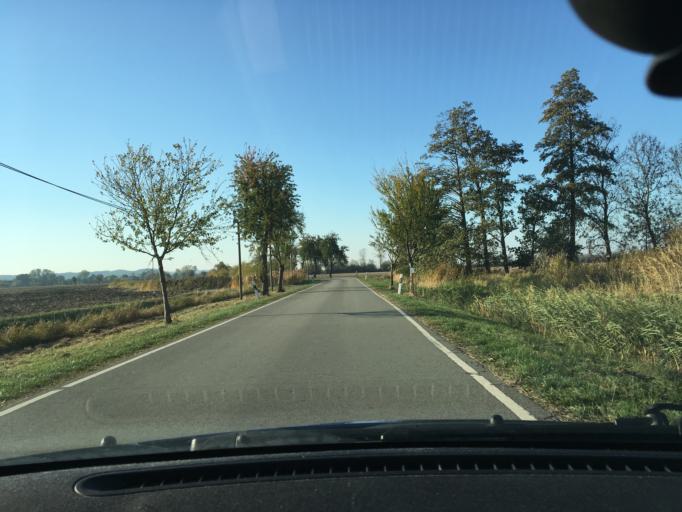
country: DE
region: Lower Saxony
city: Hitzacker
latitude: 53.1846
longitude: 11.0324
